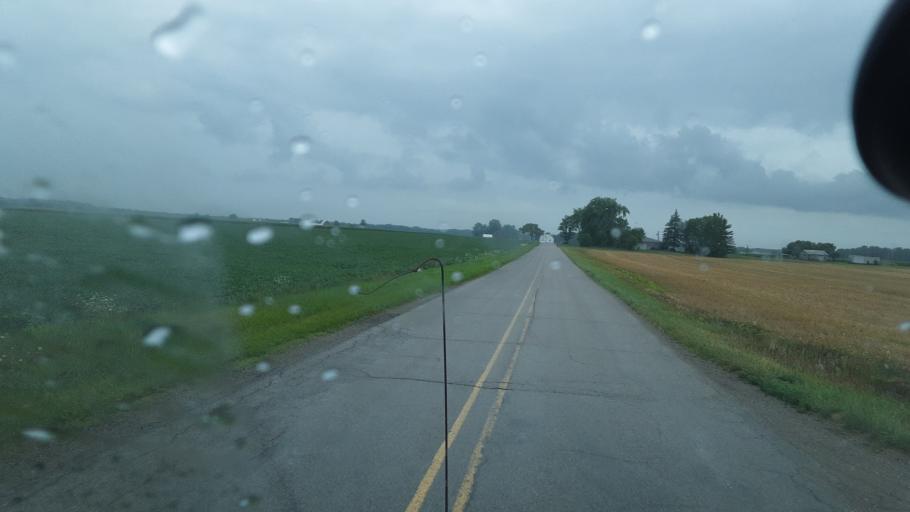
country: US
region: Ohio
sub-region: Williams County
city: Edgerton
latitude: 41.5004
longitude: -84.8045
